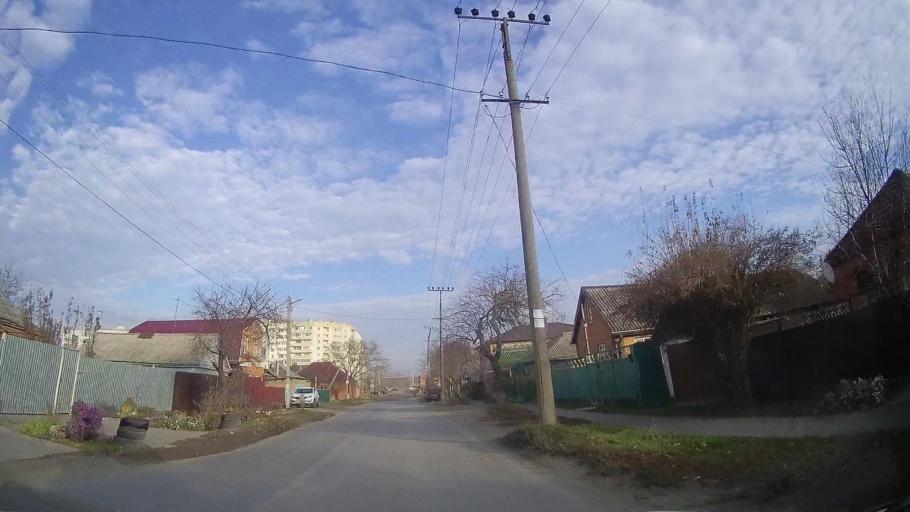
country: RU
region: Rostov
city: Bataysk
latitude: 47.1329
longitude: 39.7737
